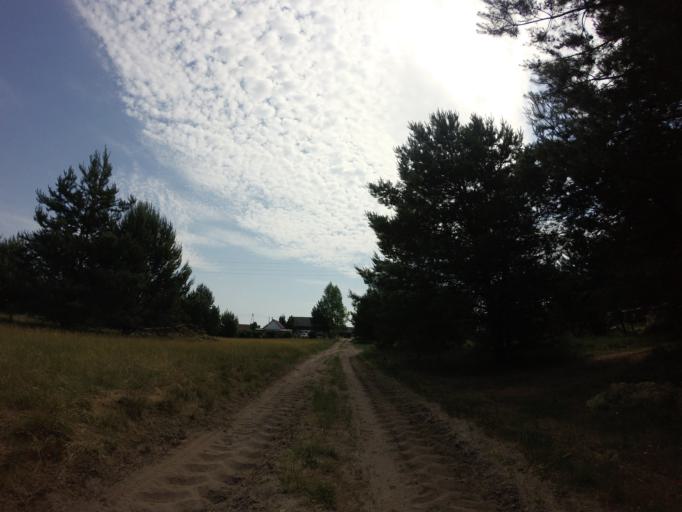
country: PL
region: Lubusz
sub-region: Powiat strzelecko-drezdenecki
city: Dobiegniew
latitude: 53.0853
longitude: 15.7785
